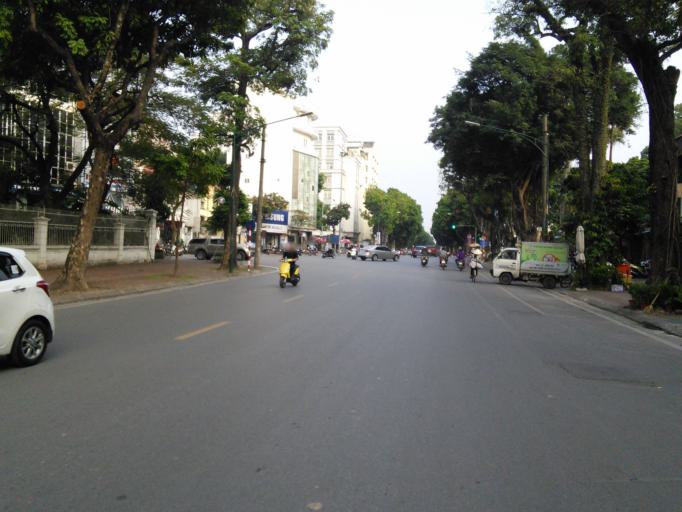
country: VN
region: Ha Noi
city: Hoan Kiem
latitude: 21.0218
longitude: 105.8494
